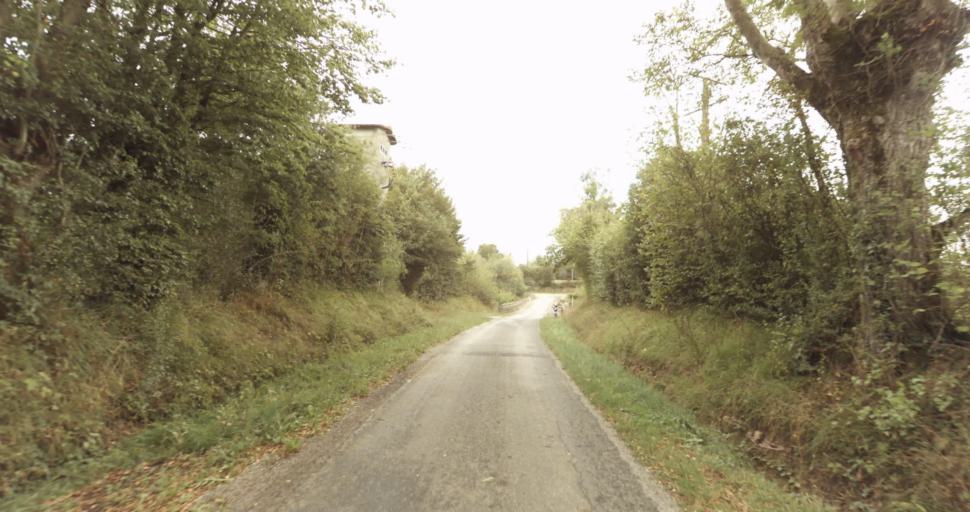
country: FR
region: Lower Normandy
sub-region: Departement de l'Orne
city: Gace
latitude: 48.7083
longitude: 0.3362
